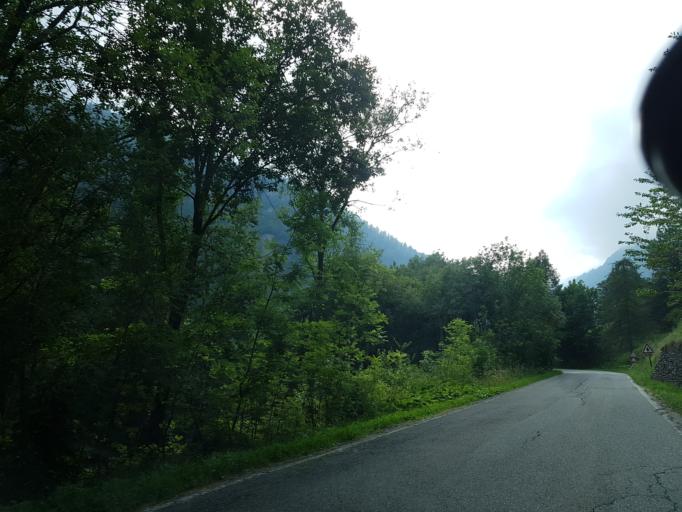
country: IT
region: Piedmont
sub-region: Provincia di Cuneo
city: Casteldelfino
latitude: 44.5857
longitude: 7.0563
